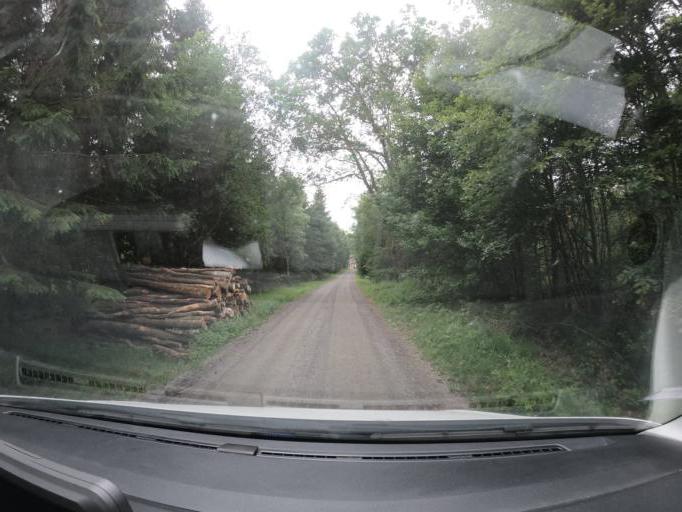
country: SE
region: Skane
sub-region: Hassleholms Kommun
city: Sosdala
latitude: 56.0944
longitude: 13.5837
